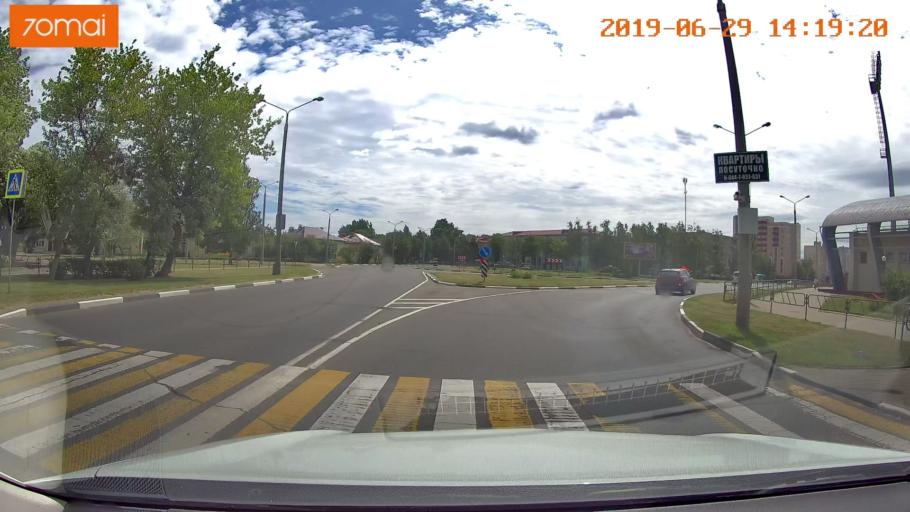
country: BY
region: Minsk
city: Salihorsk
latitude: 52.7993
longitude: 27.5404
